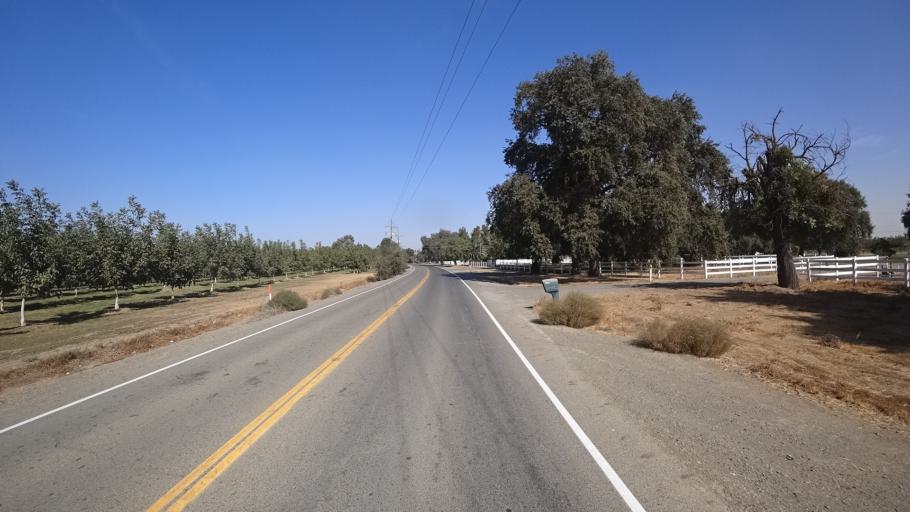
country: US
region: California
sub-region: Yolo County
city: Davis
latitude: 38.5250
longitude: -121.6949
